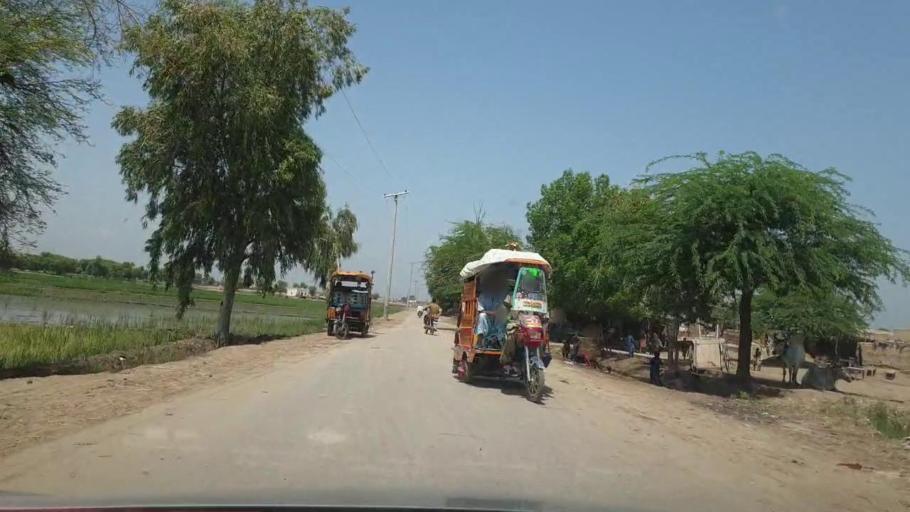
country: PK
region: Sindh
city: Warah
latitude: 27.4794
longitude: 67.7562
